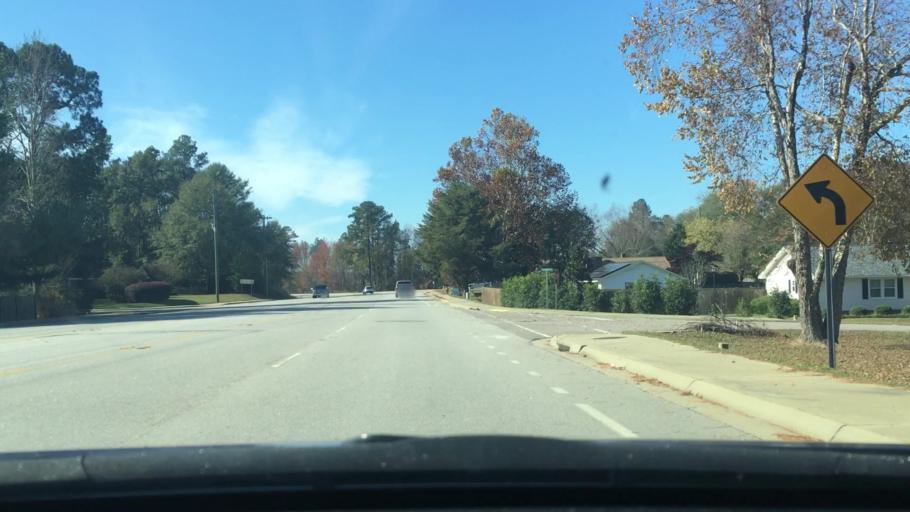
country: US
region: South Carolina
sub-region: Sumter County
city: Cane Savannah
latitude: 33.8960
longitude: -80.4057
